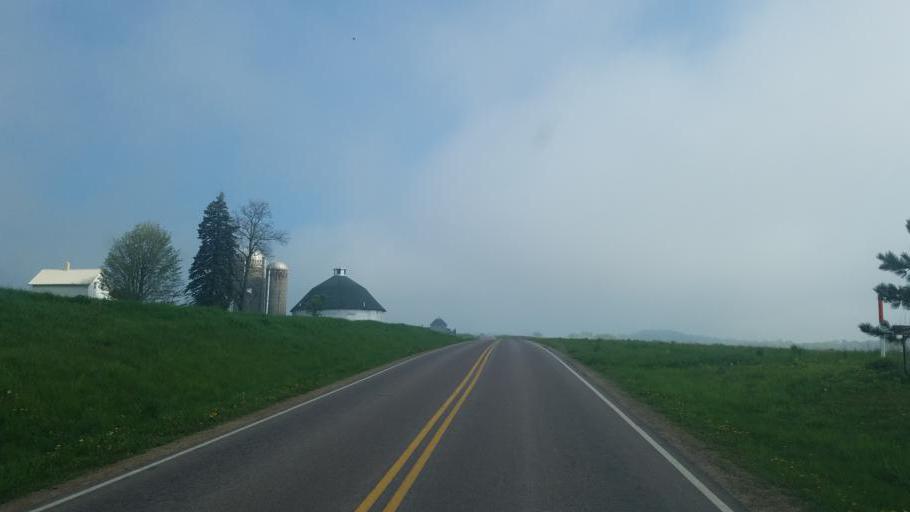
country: US
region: Wisconsin
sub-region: Vernon County
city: Hillsboro
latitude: 43.6400
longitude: -90.3526
